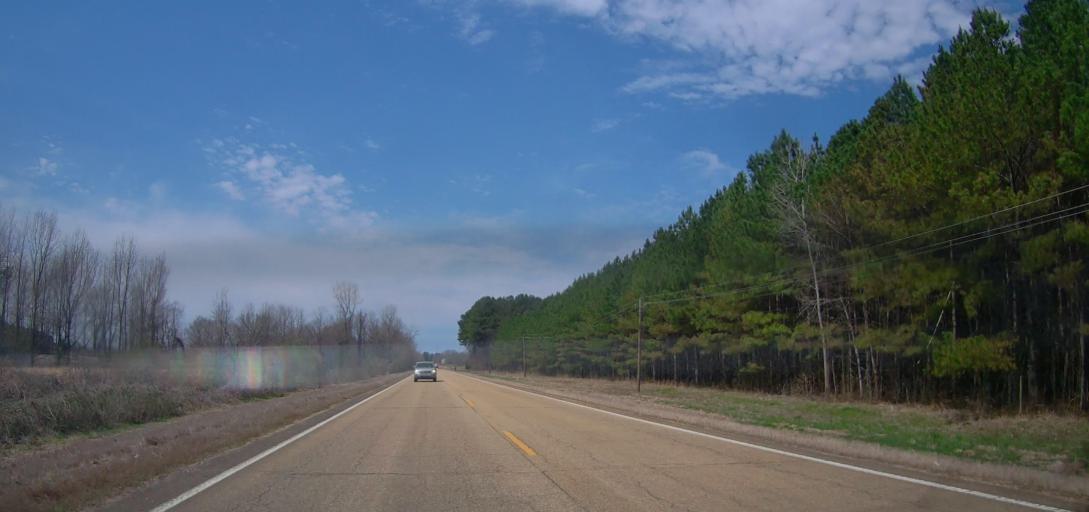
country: US
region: Mississippi
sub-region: Union County
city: New Albany
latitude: 34.6147
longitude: -89.1582
